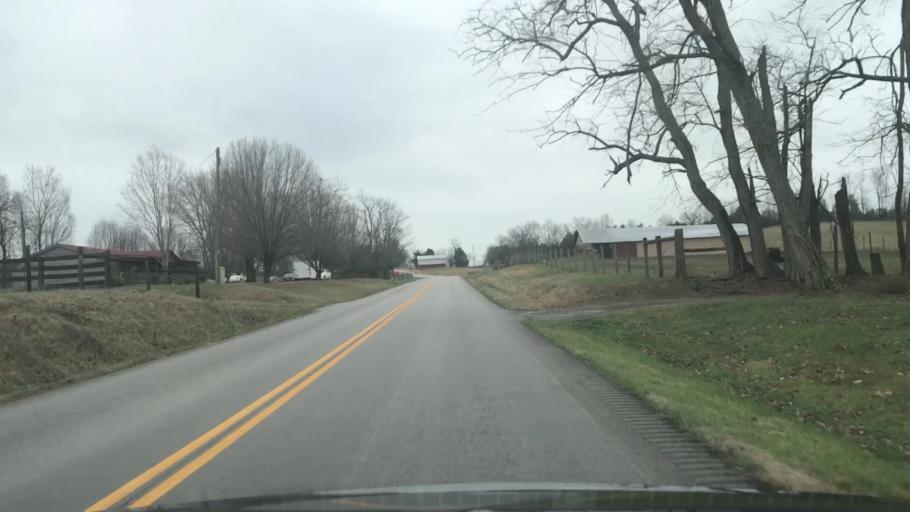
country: US
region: Kentucky
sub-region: Barren County
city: Glasgow
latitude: 36.9097
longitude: -85.7987
